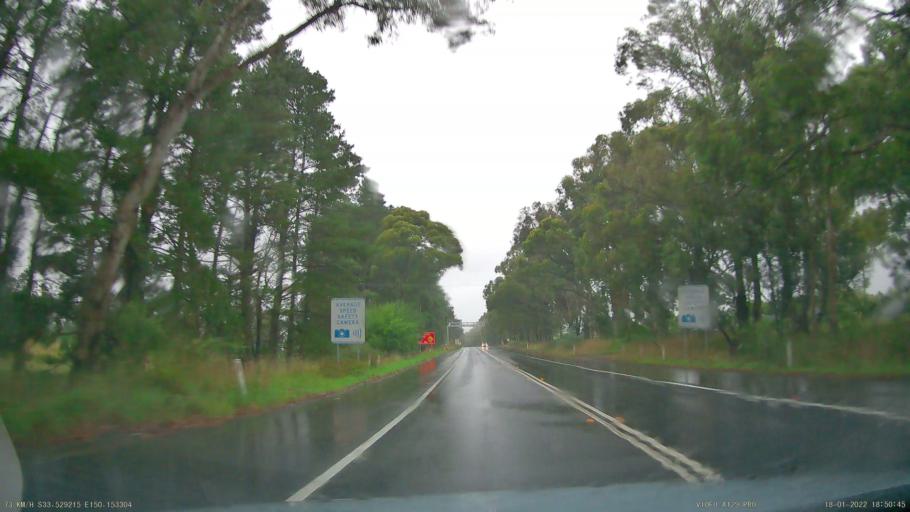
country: AU
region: New South Wales
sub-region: Lithgow
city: Bowenfels
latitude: -33.5295
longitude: 150.1533
